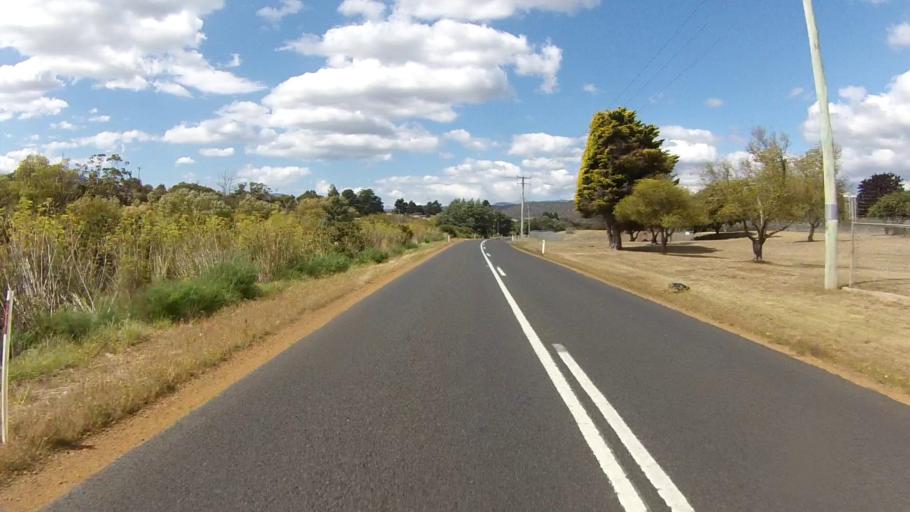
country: AU
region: Tasmania
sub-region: Derwent Valley
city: New Norfolk
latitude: -42.7671
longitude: 147.0215
